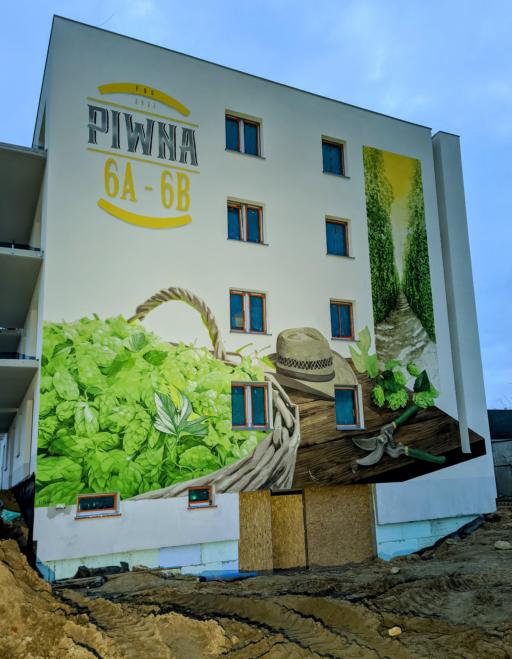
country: PL
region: Lubusz
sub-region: Zielona Gora
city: Zielona Gora
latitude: 51.9275
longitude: 15.5096
